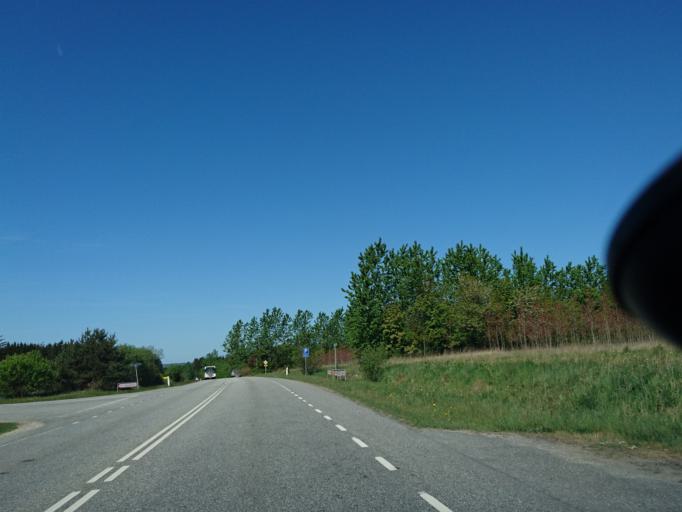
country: DK
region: North Denmark
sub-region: Hjorring Kommune
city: Sindal
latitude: 57.4616
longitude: 10.3044
